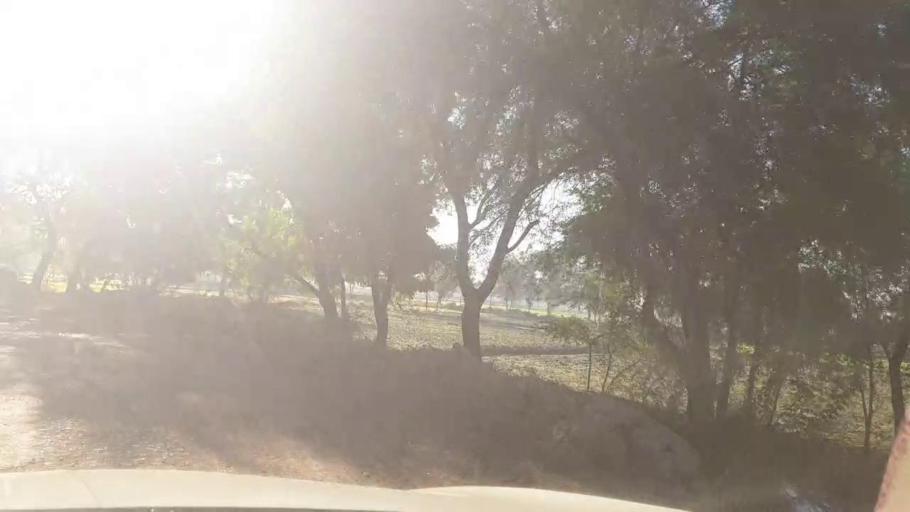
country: PK
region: Sindh
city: Bhan
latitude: 26.5452
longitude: 67.6749
